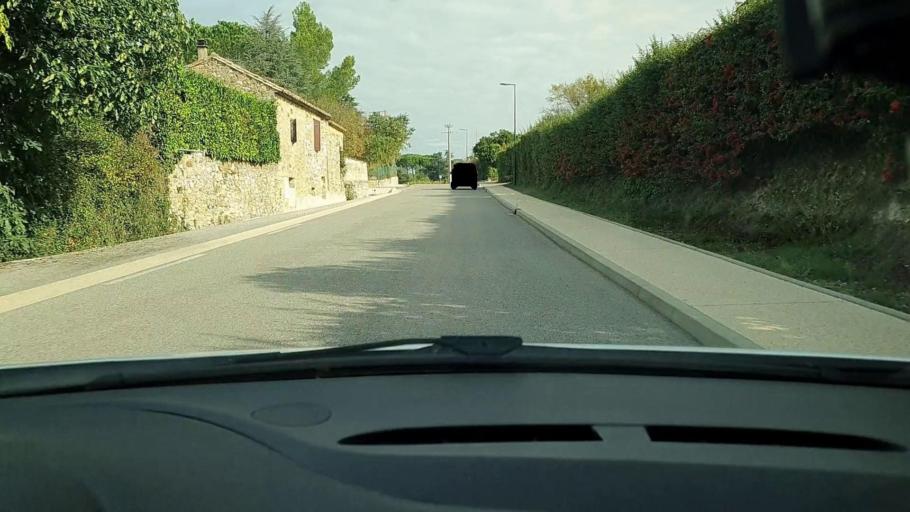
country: FR
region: Languedoc-Roussillon
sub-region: Departement du Gard
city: Saint-Quentin-la-Poterie
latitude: 44.1018
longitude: 4.4550
